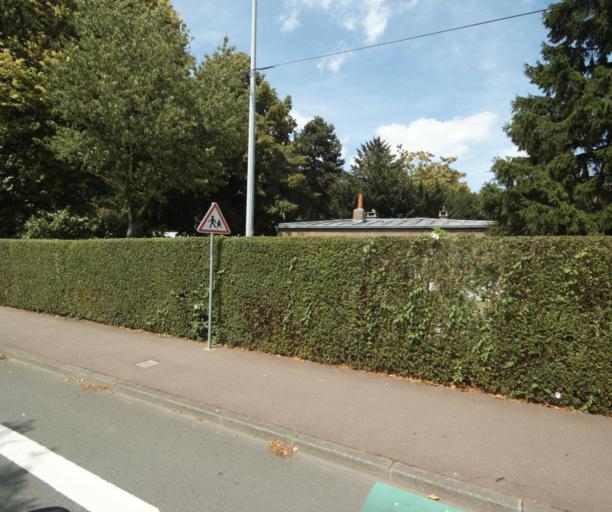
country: FR
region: Nord-Pas-de-Calais
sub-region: Departement du Nord
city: Mons-en-Baroeul
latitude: 50.6422
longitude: 3.1020
